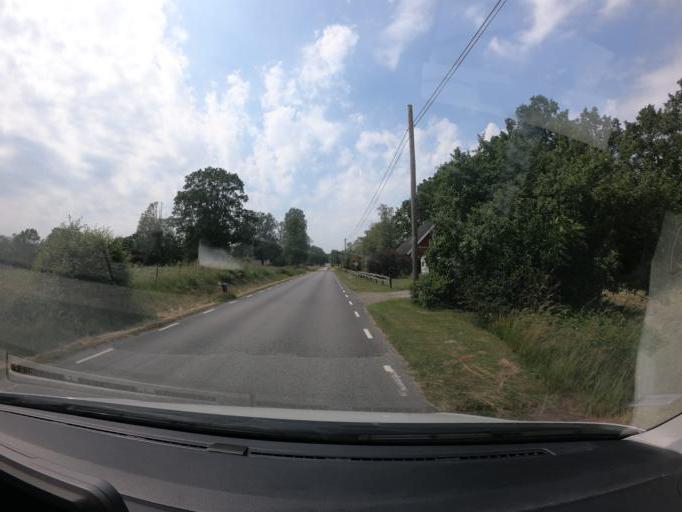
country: SE
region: Skane
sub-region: Hassleholms Kommun
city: Bjarnum
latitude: 56.2835
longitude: 13.6458
